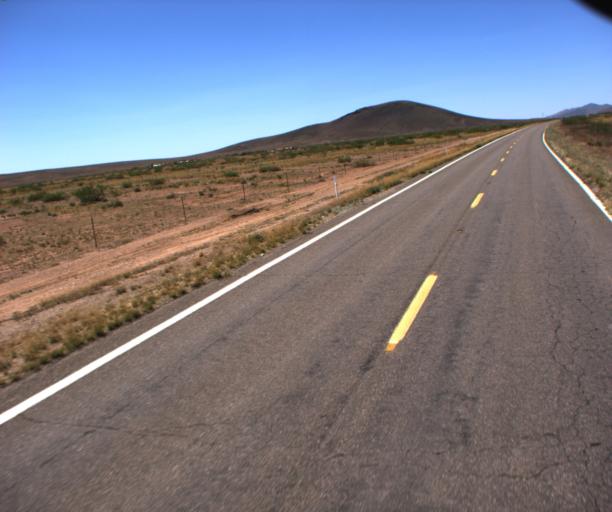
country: US
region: Arizona
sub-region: Cochise County
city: Douglas
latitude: 31.6417
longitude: -109.1753
